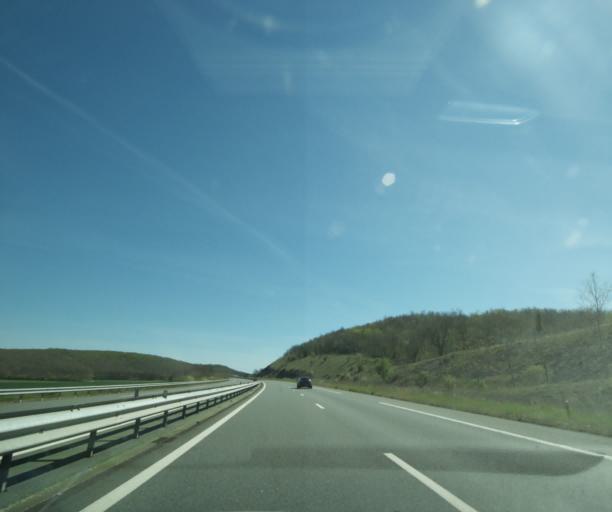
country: FR
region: Midi-Pyrenees
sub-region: Departement du Lot
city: Le Vigan
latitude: 44.7806
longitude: 1.5318
